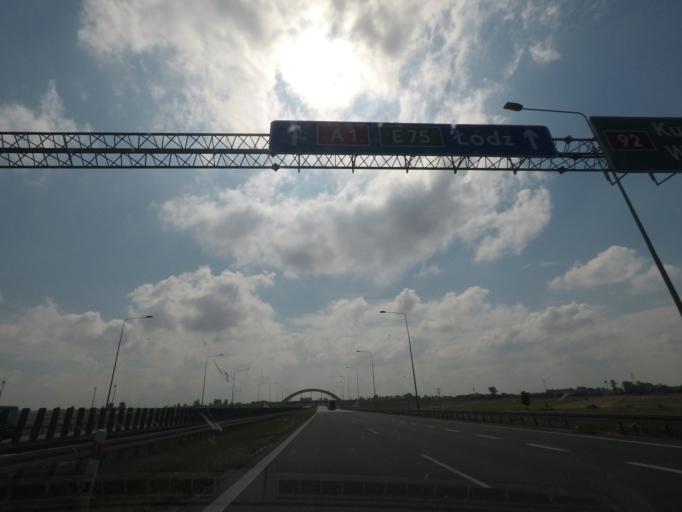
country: PL
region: Lodz Voivodeship
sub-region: Powiat kutnowski
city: Krzyzanow
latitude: 52.2274
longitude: 19.4620
